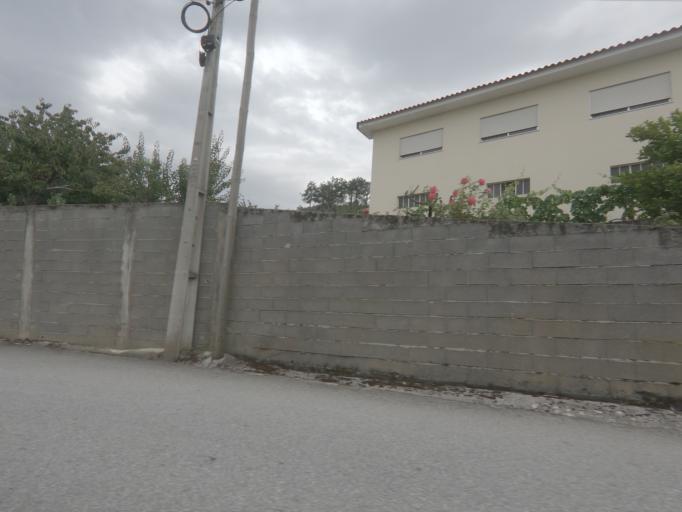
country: PT
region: Viseu
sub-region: Armamar
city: Armamar
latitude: 41.1218
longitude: -7.6632
